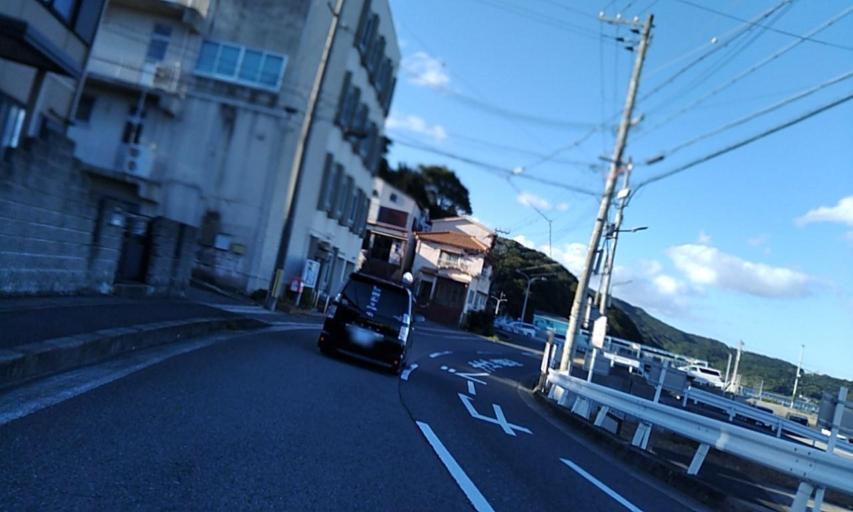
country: JP
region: Wakayama
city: Minato
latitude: 34.3134
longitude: 135.0948
